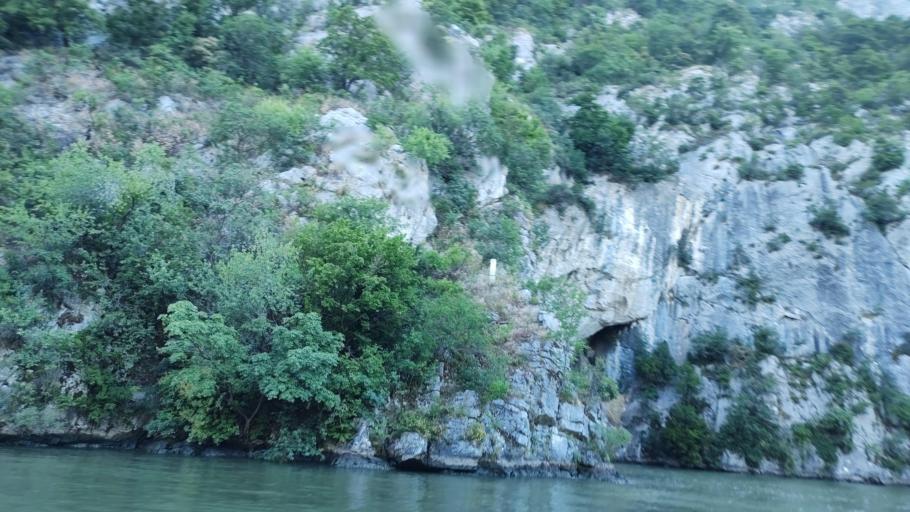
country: RO
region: Mehedinti
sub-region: Comuna Dubova
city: Dubova
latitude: 44.5949
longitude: 22.2617
